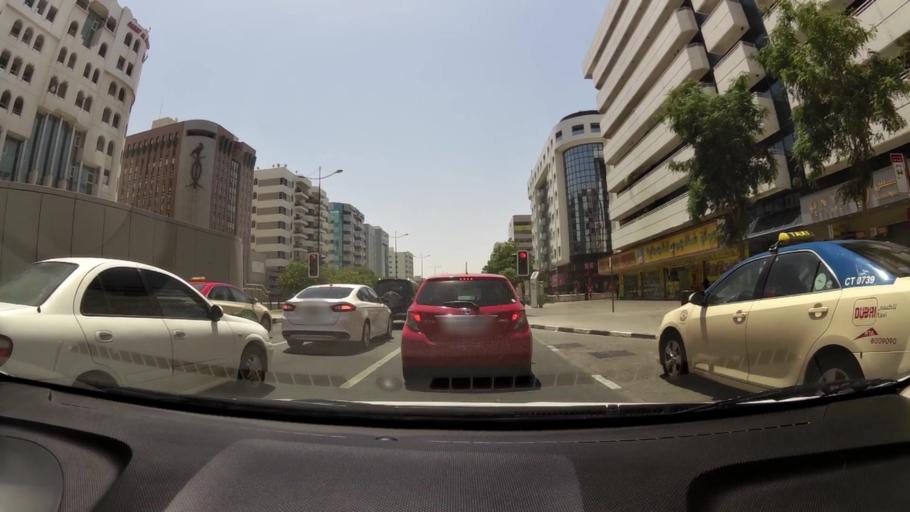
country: AE
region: Ash Shariqah
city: Sharjah
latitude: 25.2630
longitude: 55.3244
